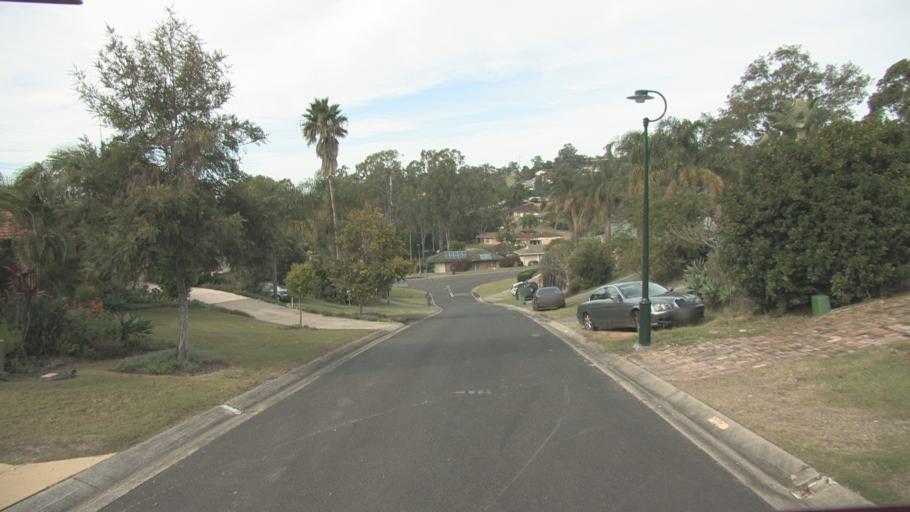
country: AU
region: Queensland
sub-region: Logan
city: Beenleigh
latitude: -27.7026
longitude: 153.1764
